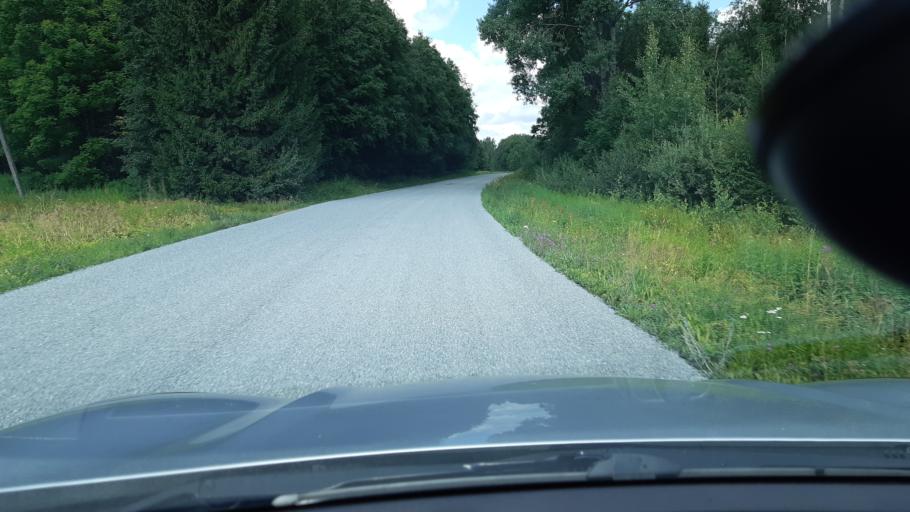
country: EE
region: Raplamaa
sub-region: Kehtna vald
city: Kehtna
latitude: 58.8959
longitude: 25.0267
